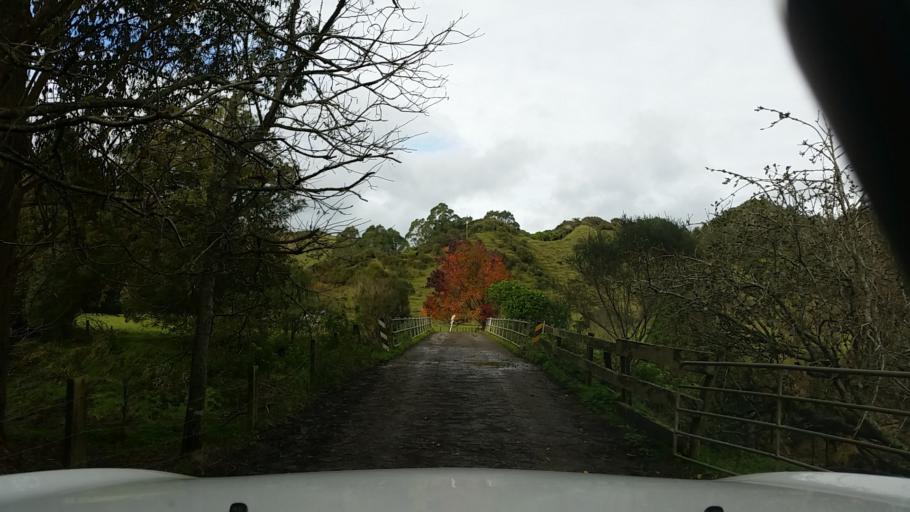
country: NZ
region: Taranaki
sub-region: New Plymouth District
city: Waitara
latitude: -38.8150
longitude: 174.6170
